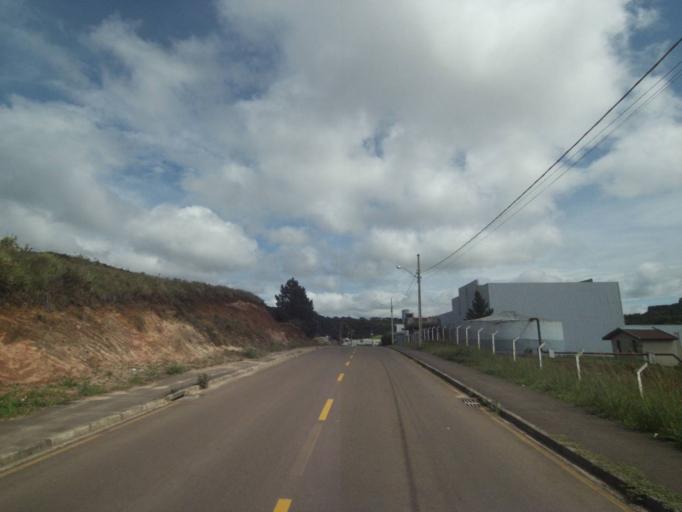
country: BR
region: Parana
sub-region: Quatro Barras
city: Quatro Barras
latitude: -25.3485
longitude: -49.0733
